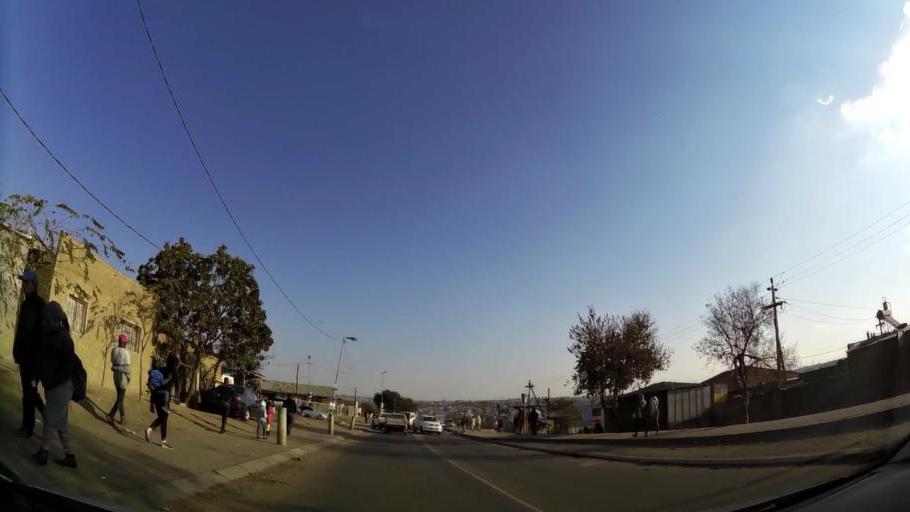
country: ZA
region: Gauteng
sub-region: Ekurhuleni Metropolitan Municipality
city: Tembisa
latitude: -25.9969
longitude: 28.1980
